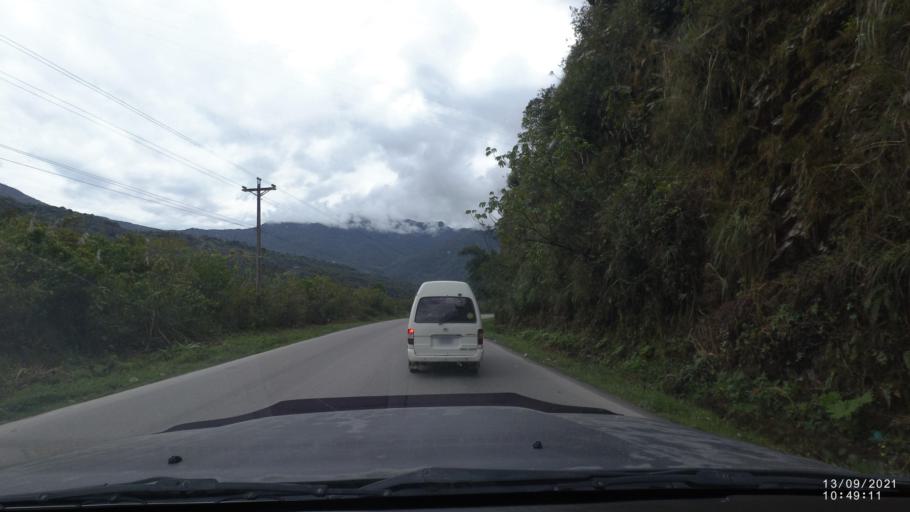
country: BO
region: Cochabamba
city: Colomi
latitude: -17.2026
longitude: -65.8571
